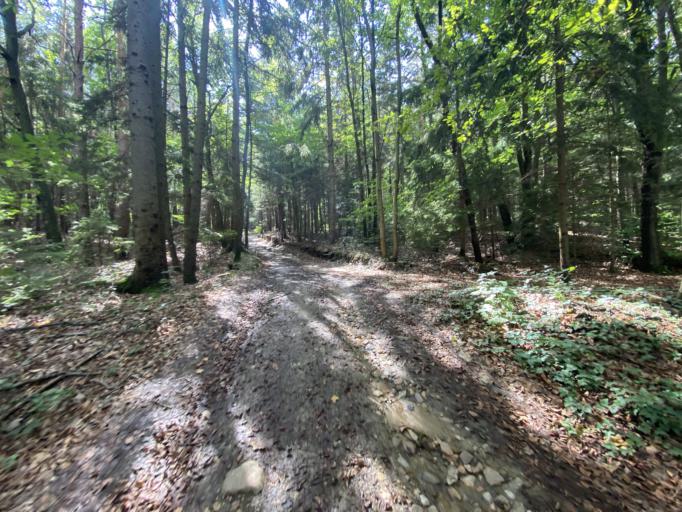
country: AT
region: Burgenland
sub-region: Politischer Bezirk Oberpullendorf
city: Kobersdorf
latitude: 47.5827
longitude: 16.3822
